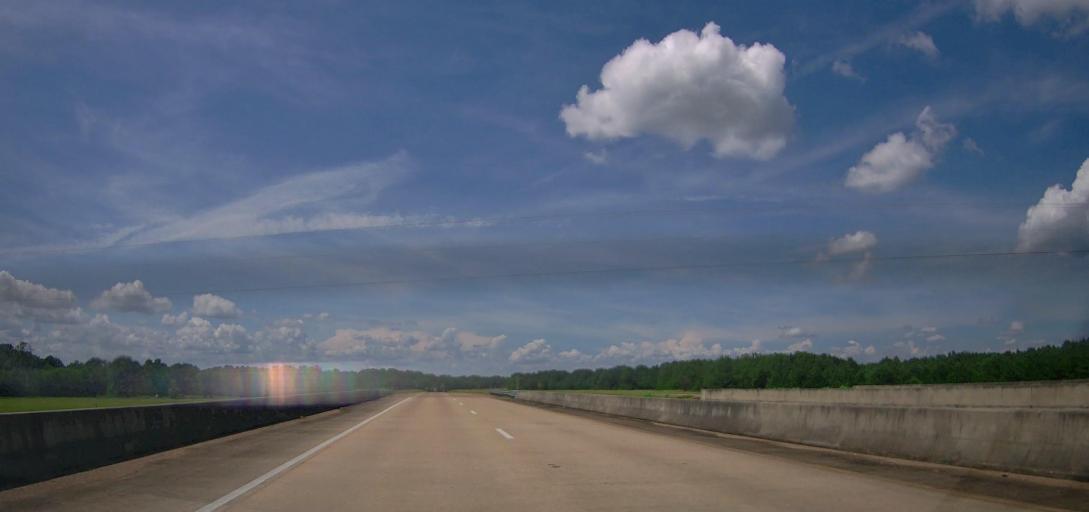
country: US
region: Mississippi
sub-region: Monroe County
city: Aberdeen
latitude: 33.8399
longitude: -88.5916
